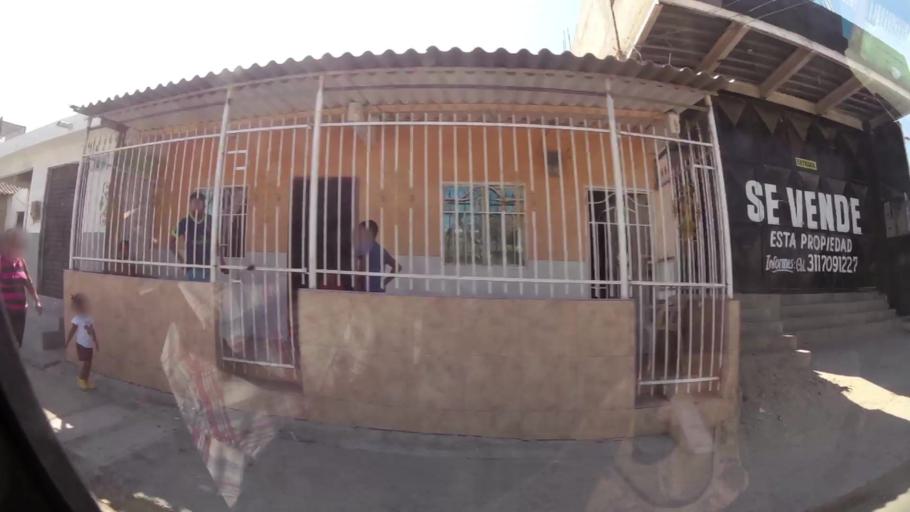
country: CO
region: Bolivar
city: Cartagena
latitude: 10.4183
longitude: -75.5198
